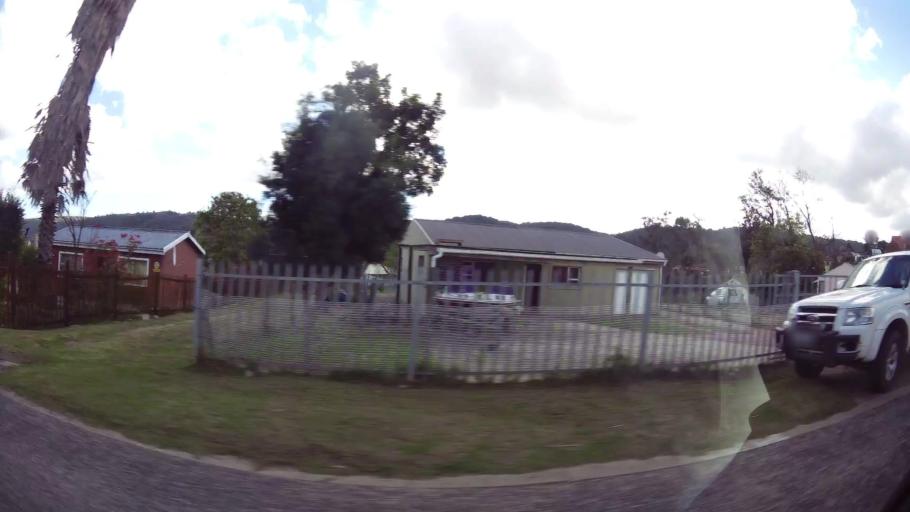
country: ZA
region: Western Cape
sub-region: Eden District Municipality
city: Knysna
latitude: -34.0461
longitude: 23.0842
